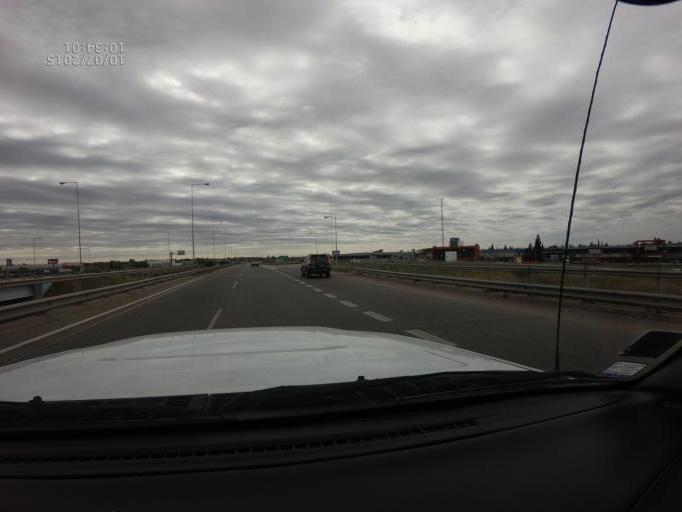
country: AR
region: Cordoba
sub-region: Departamento de Capital
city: Cordoba
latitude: -31.3542
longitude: -64.2025
